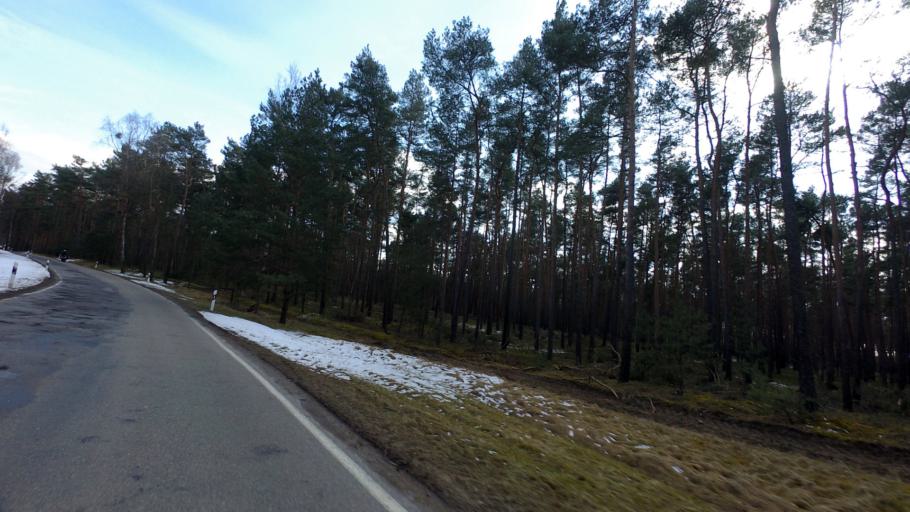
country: DE
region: Brandenburg
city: Marienwerder
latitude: 52.8002
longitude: 13.5922
